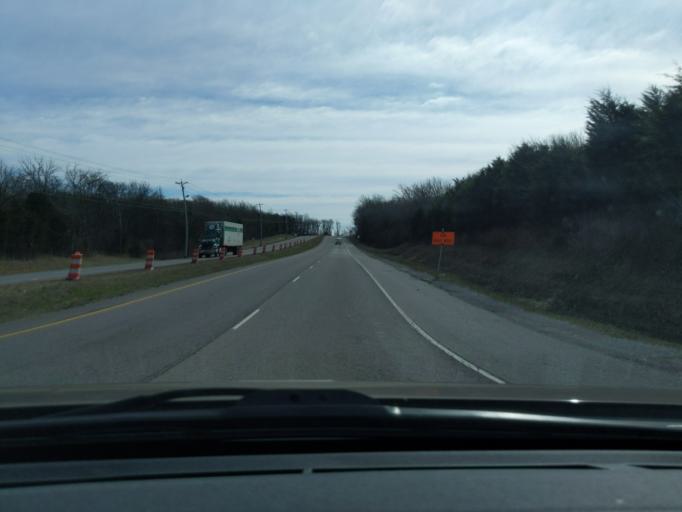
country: US
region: Tennessee
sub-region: Wilson County
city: Mount Juliet
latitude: 36.1846
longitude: -86.4617
